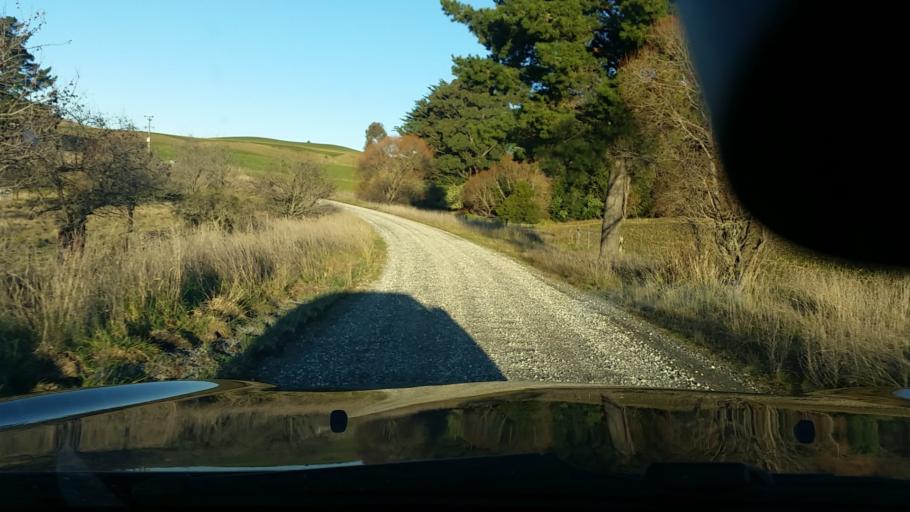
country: NZ
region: Marlborough
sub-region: Marlborough District
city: Blenheim
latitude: -41.7381
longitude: 174.0426
